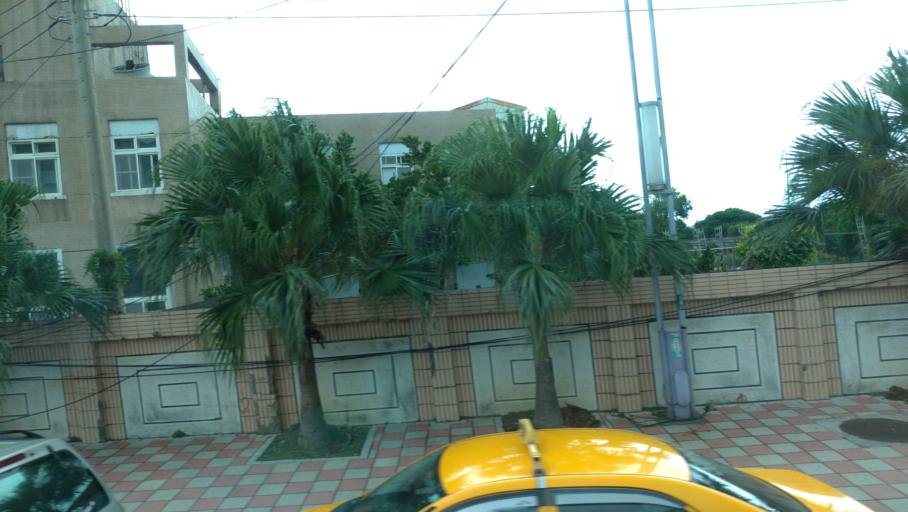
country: TW
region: Taiwan
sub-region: Keelung
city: Keelung
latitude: 25.1510
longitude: 121.7747
